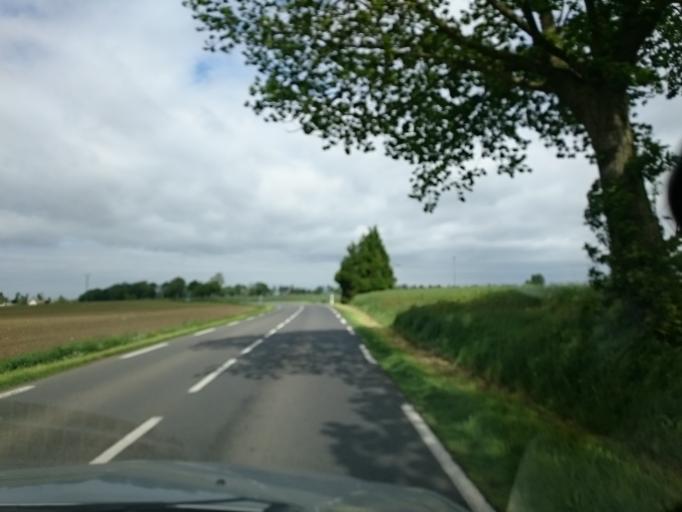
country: FR
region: Lower Normandy
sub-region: Departement de la Manche
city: Saint-James
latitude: 48.5430
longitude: -1.3688
